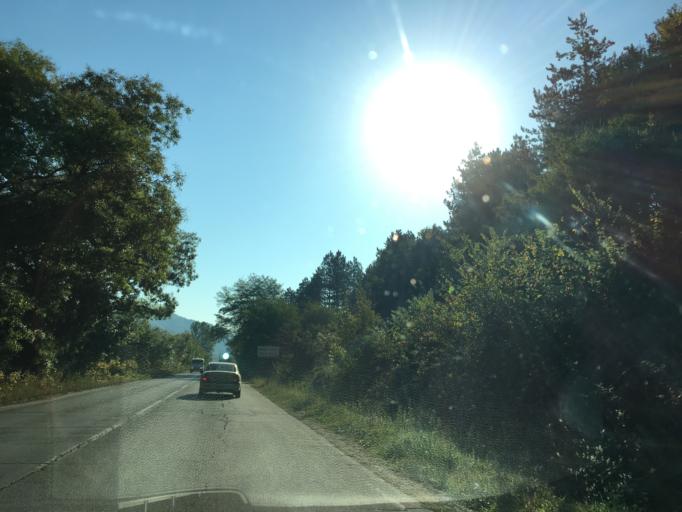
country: BG
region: Pazardzhik
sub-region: Obshtina Belovo
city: Belovo
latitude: 42.2304
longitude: 23.9625
